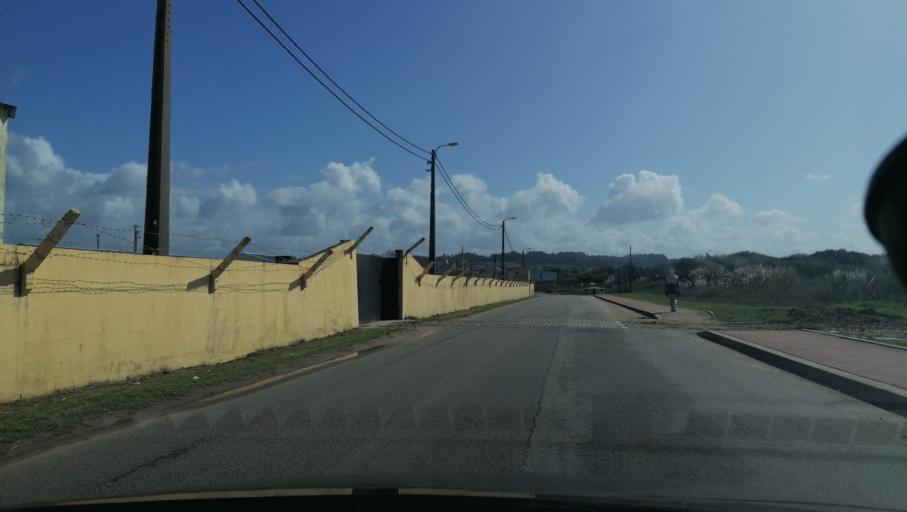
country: PT
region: Aveiro
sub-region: Ovar
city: Esmoriz
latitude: 40.9752
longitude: -8.6428
